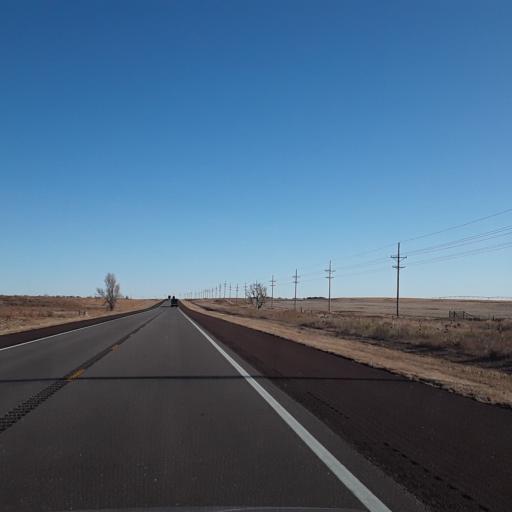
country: US
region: Kansas
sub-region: Meade County
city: Plains
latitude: 37.1871
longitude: -100.7138
